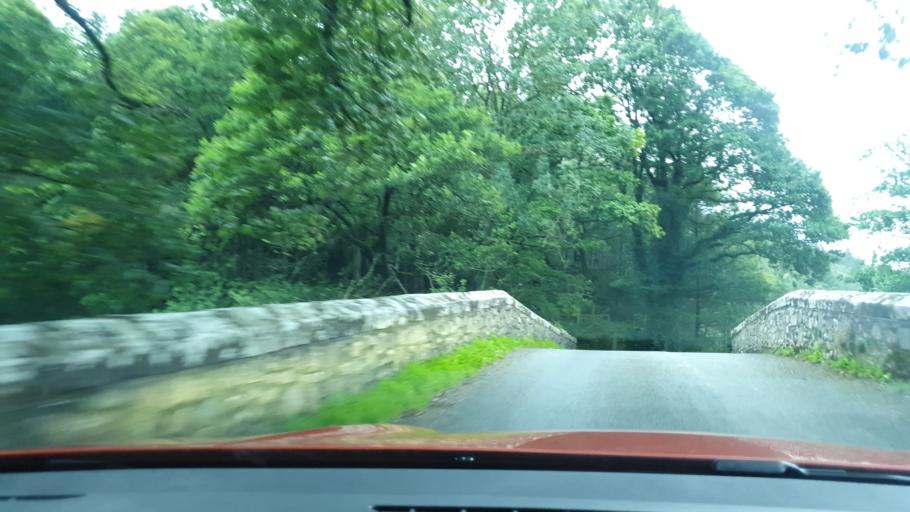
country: GB
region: England
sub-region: Cumbria
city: Seascale
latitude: 54.3842
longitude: -3.3115
